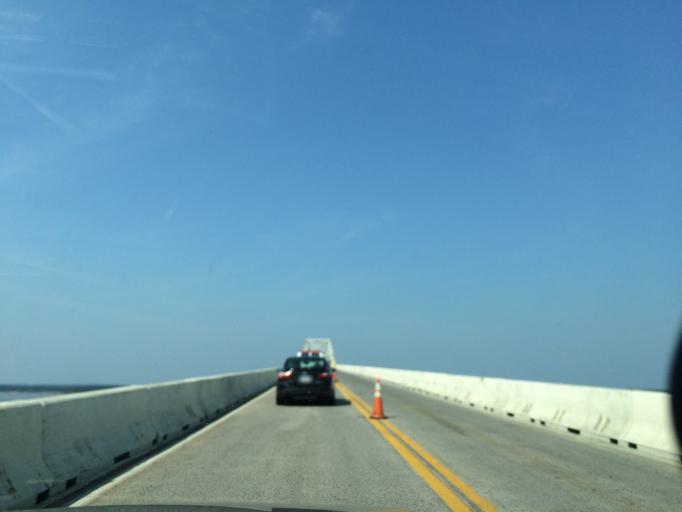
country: US
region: Virginia
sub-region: King George County
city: Dahlgren
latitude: 38.3631
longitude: -76.9860
